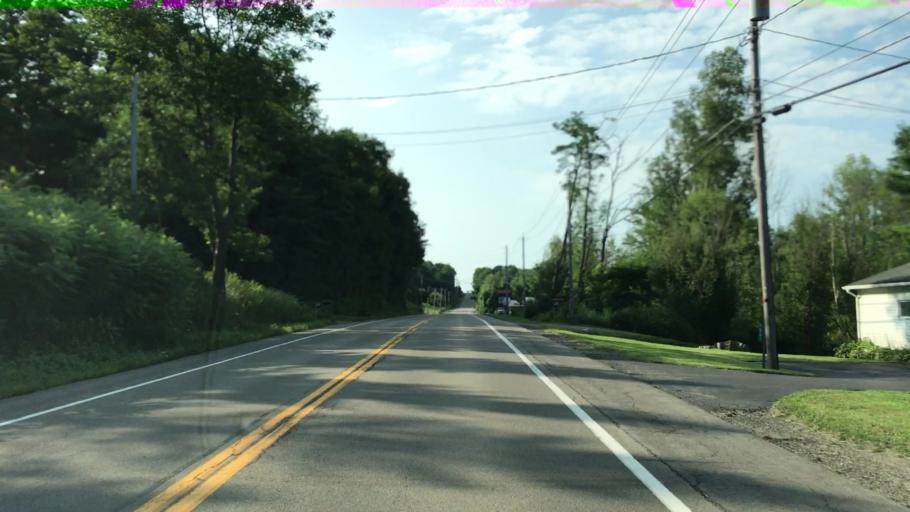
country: US
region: New York
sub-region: Chautauqua County
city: Mayville
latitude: 42.2553
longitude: -79.4669
